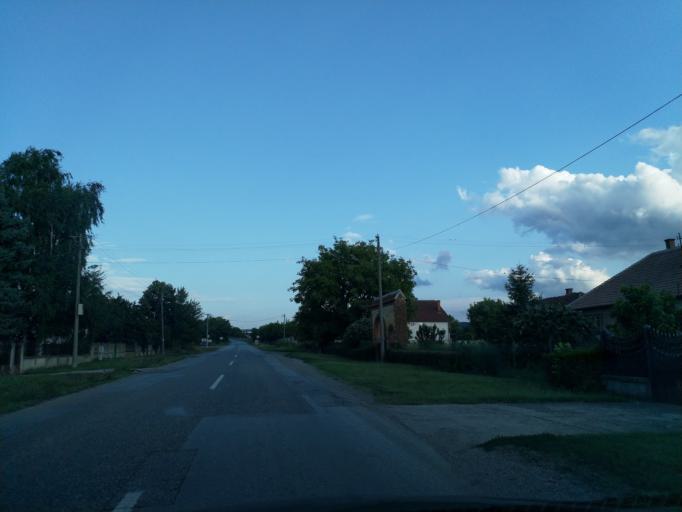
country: RS
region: Central Serbia
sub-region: Rasinski Okrug
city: Cicevac
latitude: 43.7525
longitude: 21.4394
